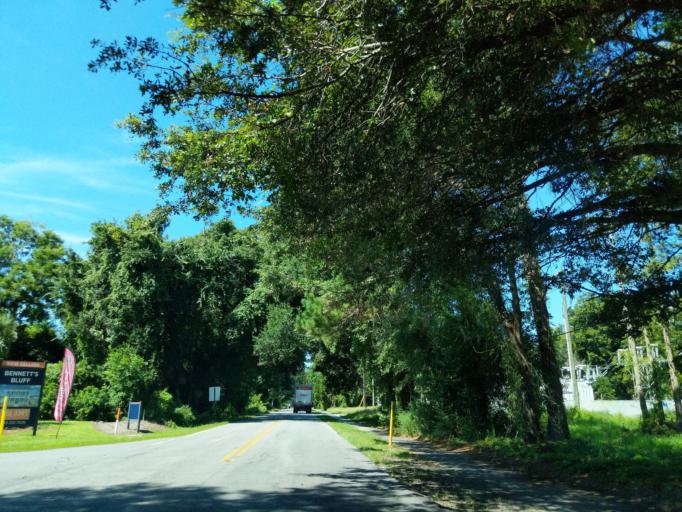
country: US
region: South Carolina
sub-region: Charleston County
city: Charleston
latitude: 32.7292
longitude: -79.9362
